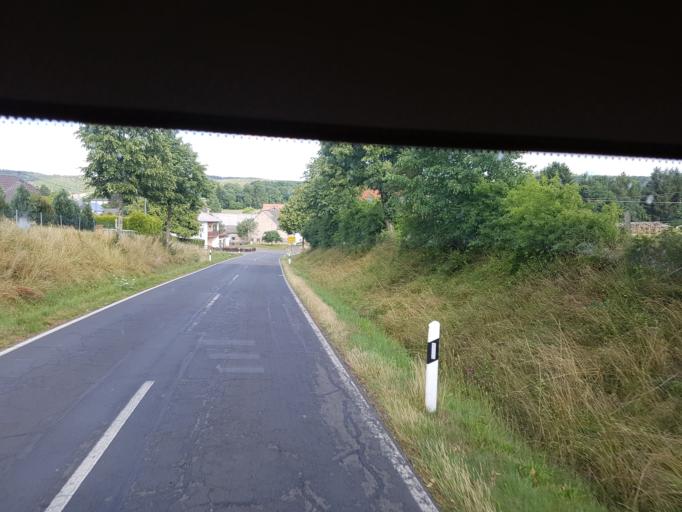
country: DE
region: Rheinland-Pfalz
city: Nerdlen
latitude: 50.2357
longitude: 6.8562
